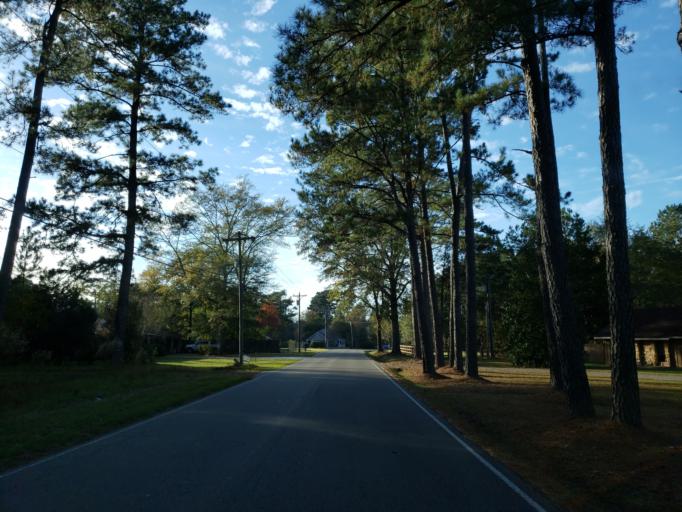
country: US
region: Mississippi
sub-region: Lamar County
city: West Hattiesburg
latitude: 31.3037
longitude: -89.3823
